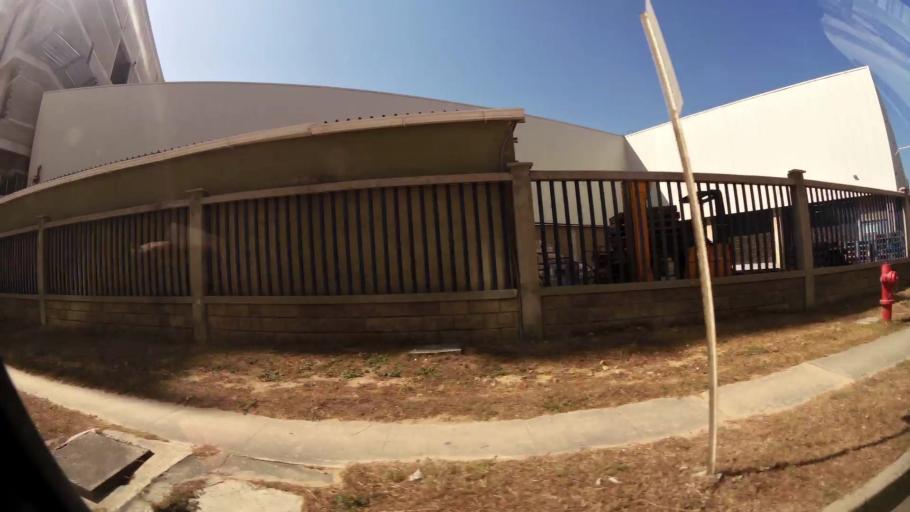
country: CO
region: Atlantico
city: Barranquilla
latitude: 11.0164
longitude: -74.8289
